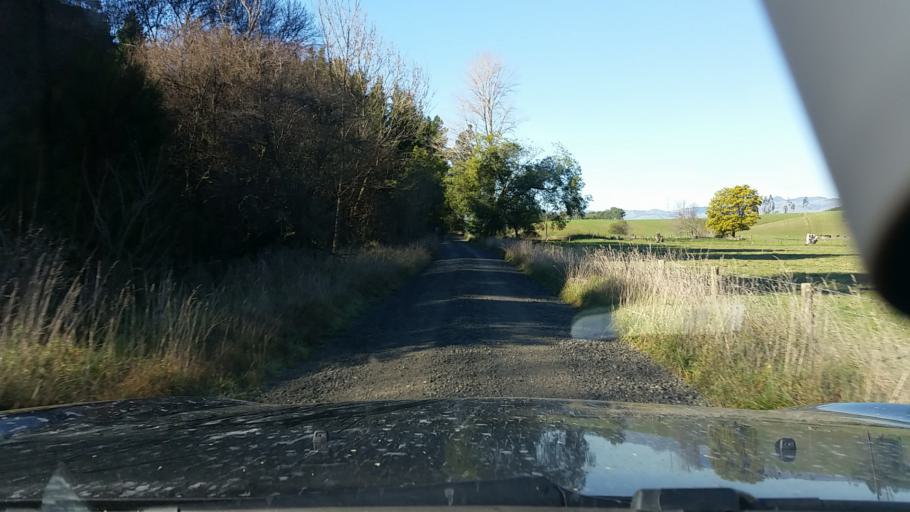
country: NZ
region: Marlborough
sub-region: Marlborough District
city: Blenheim
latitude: -41.4620
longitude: 173.7900
